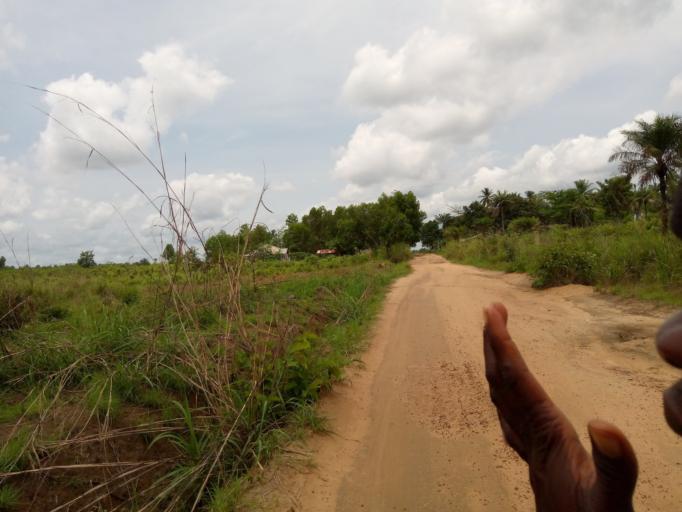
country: SL
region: Western Area
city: Waterloo
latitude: 8.3315
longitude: -12.9411
